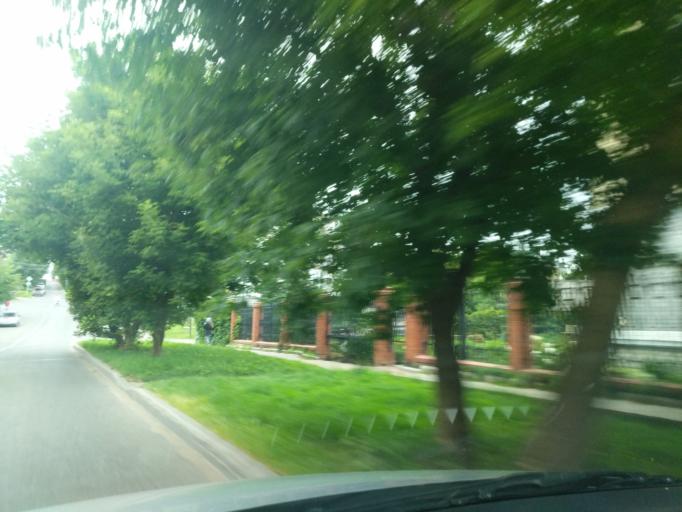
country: RU
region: Kirov
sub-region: Kirovo-Chepetskiy Rayon
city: Kirov
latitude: 58.5994
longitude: 49.6726
